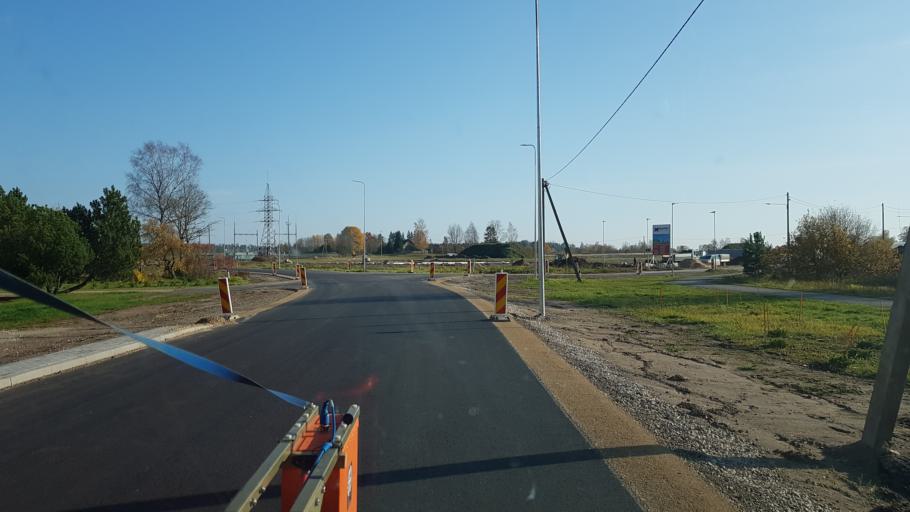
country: EE
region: Vorumaa
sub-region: Antsla vald
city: Vana-Antsla
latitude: 57.8403
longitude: 26.4814
